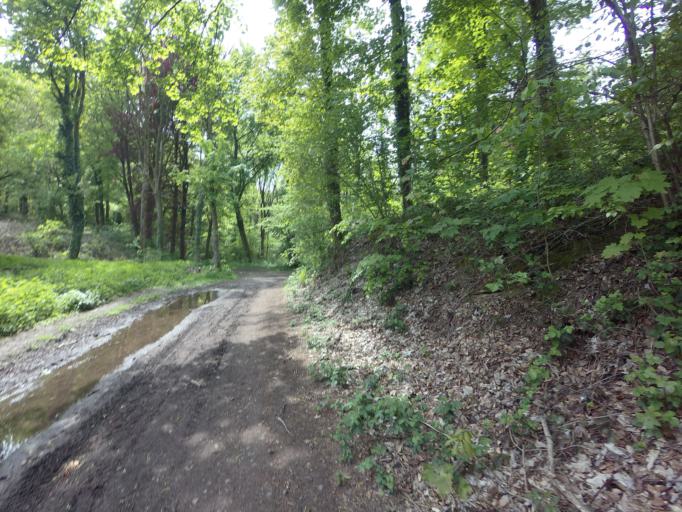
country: NL
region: Limburg
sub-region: Gemeente Maastricht
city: Heer
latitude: 50.8177
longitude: 5.7512
